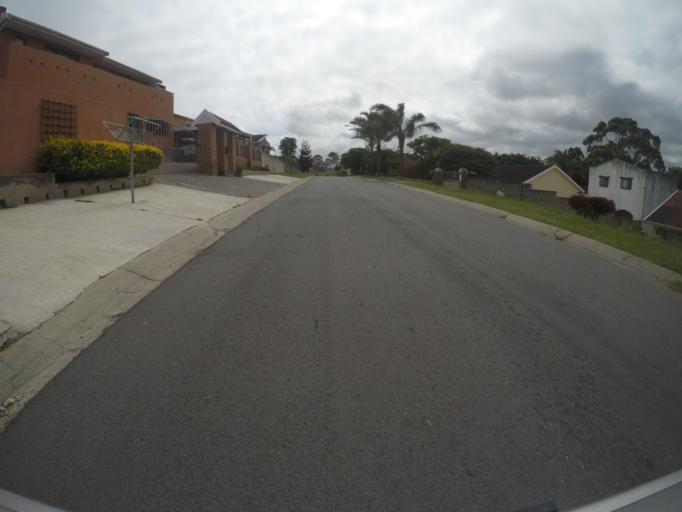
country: ZA
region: Eastern Cape
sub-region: Buffalo City Metropolitan Municipality
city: East London
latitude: -32.9990
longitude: 27.8791
